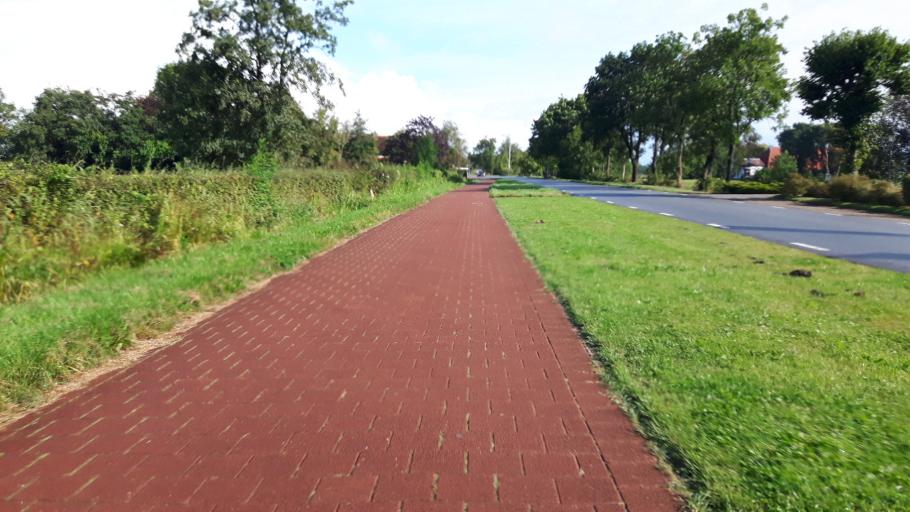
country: NL
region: Friesland
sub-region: Gemeente Smallingerland
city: Drachten
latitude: 53.0794
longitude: 6.0991
